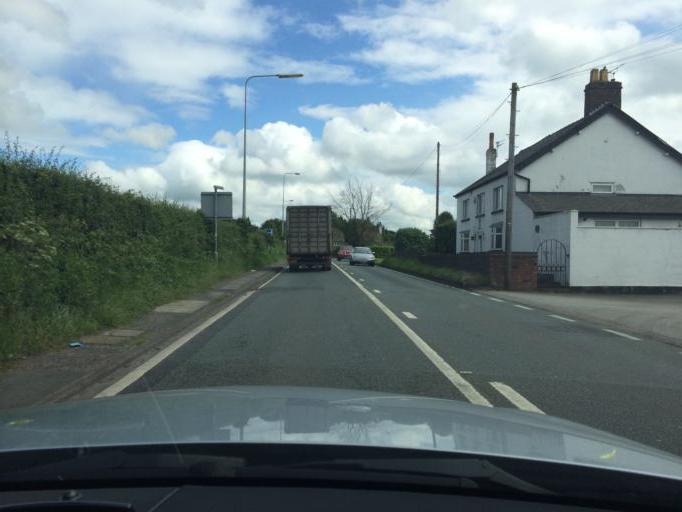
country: GB
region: England
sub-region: Cheshire East
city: Prestbury
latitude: 53.2973
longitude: -2.1374
